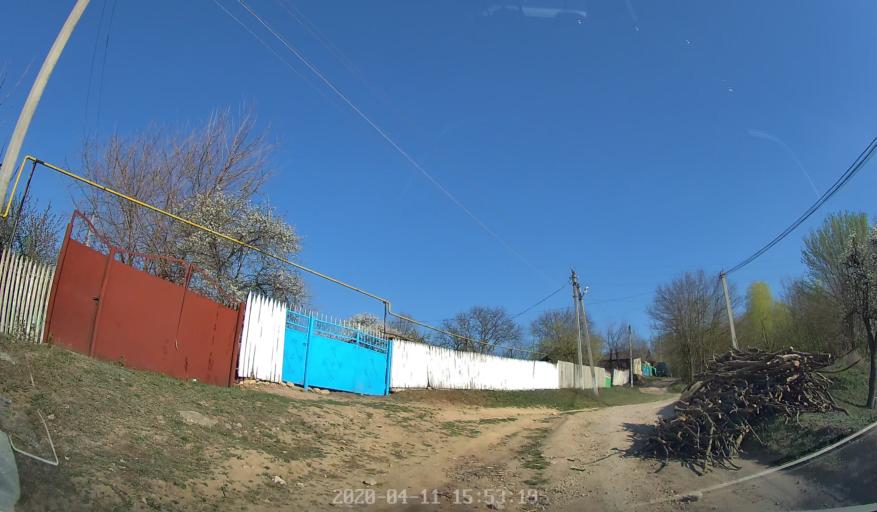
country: MD
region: Chisinau
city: Vadul lui Voda
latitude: 47.0997
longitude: 29.1773
